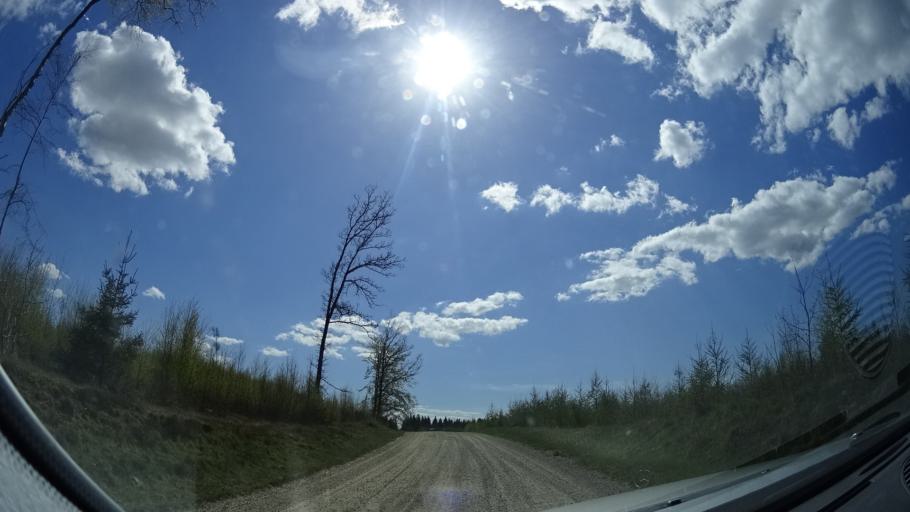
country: SE
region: Skane
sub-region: Hassleholms Kommun
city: Tormestorp
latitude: 56.0884
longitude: 13.7095
